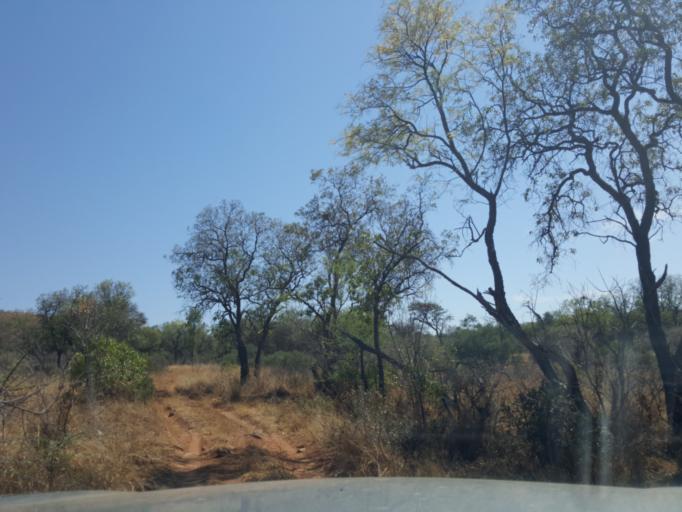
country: BW
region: South East
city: Lobatse
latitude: -25.1464
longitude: 25.6699
